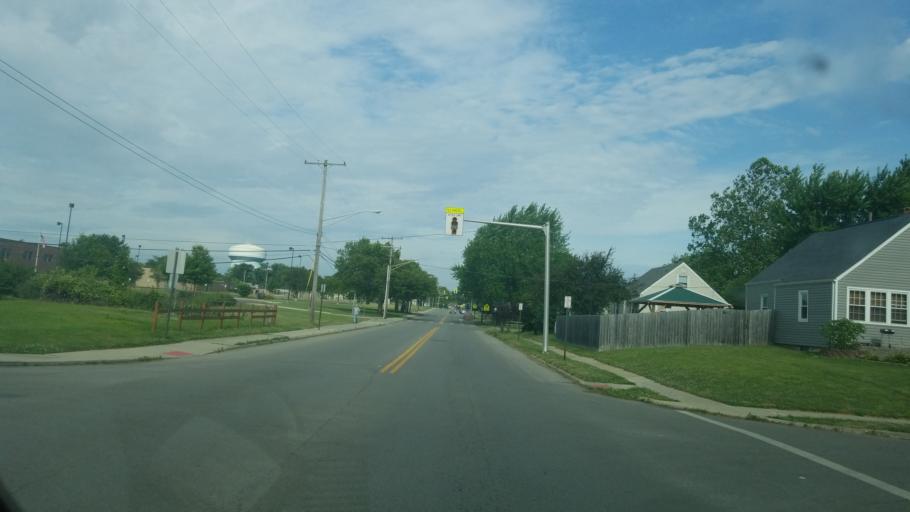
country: US
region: Ohio
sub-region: Franklin County
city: Minerva Park
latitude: 40.0355
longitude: -82.9717
